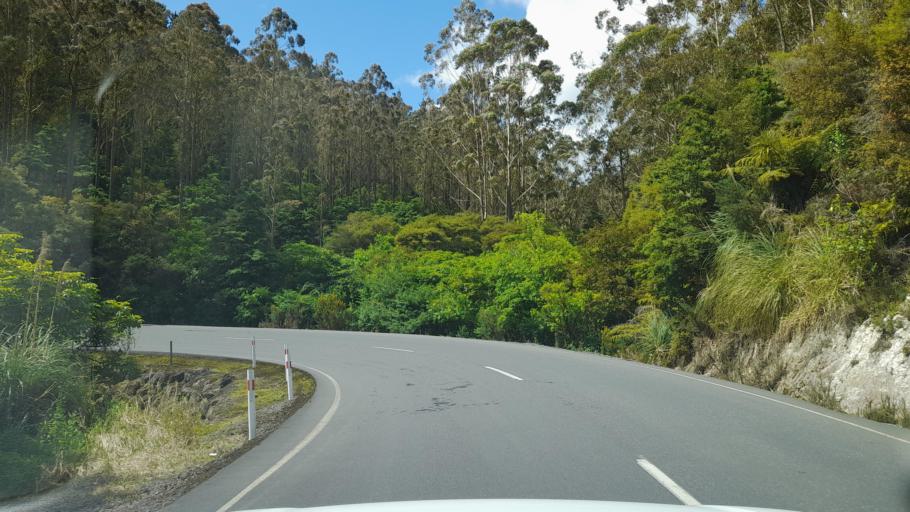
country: NZ
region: Northland
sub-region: Whangarei
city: Maungatapere
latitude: -35.6920
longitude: 174.0424
